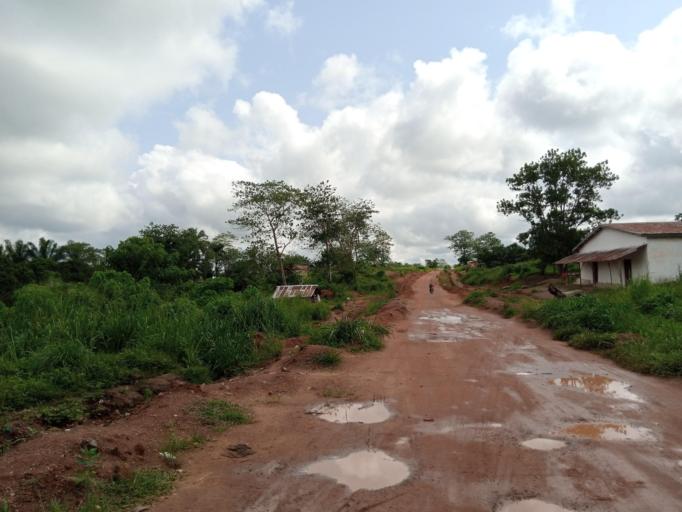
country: SL
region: Southern Province
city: Baoma
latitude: 7.9879
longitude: -11.7369
